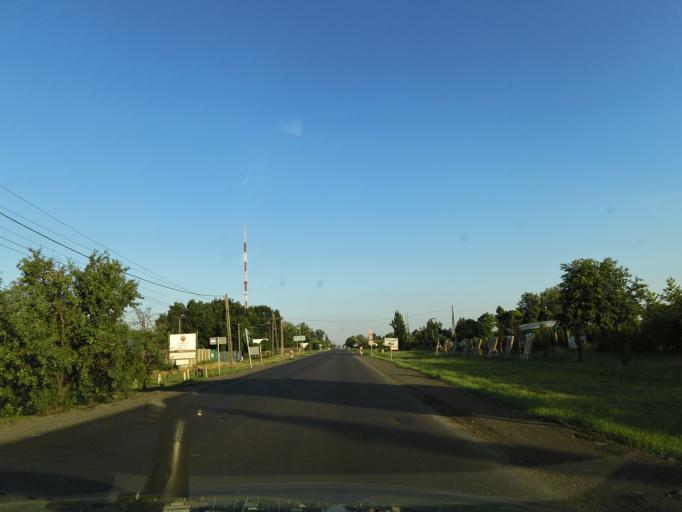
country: HU
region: Csongrad
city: Szentes
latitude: 46.6302
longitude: 20.2754
